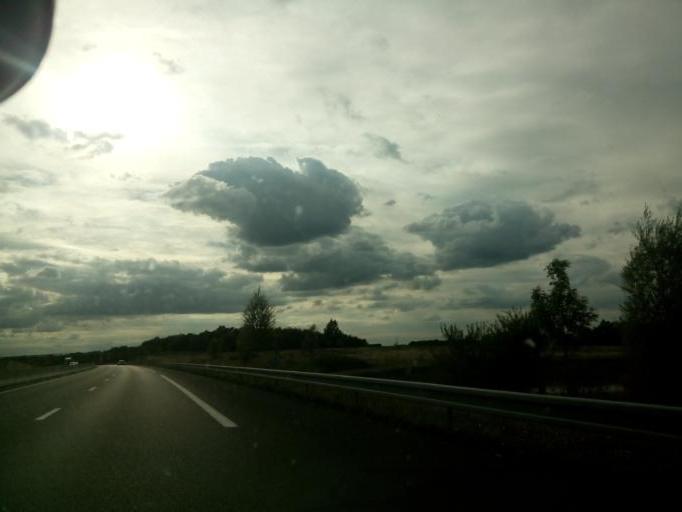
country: FR
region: Centre
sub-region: Departement du Loir-et-Cher
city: Faverolles-sur-Cher
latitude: 47.3027
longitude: 1.2116
